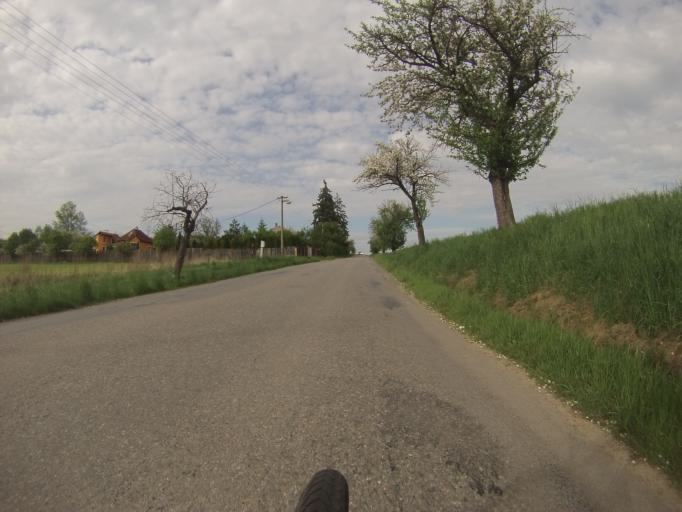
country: CZ
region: South Moravian
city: Veverska Bityska
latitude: 49.2948
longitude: 16.4542
